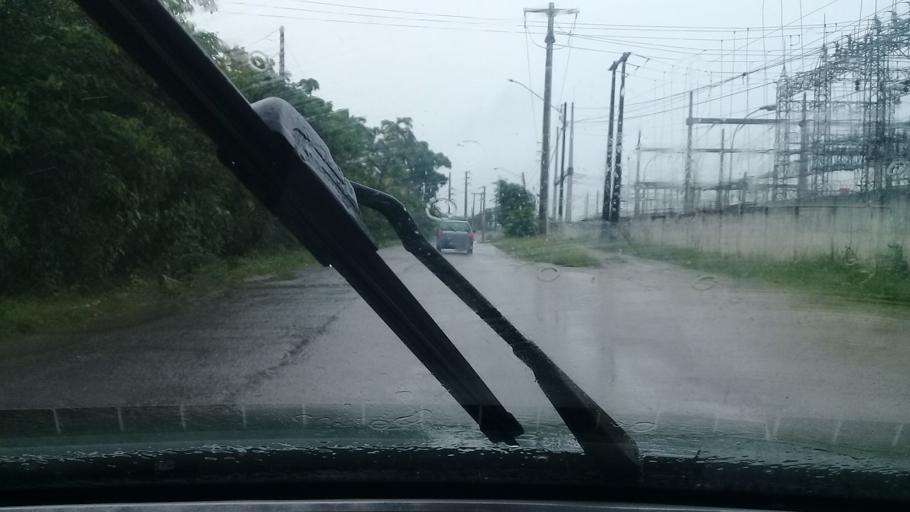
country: BR
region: Pernambuco
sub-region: Paulista
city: Paulista
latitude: -7.9554
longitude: -34.8907
